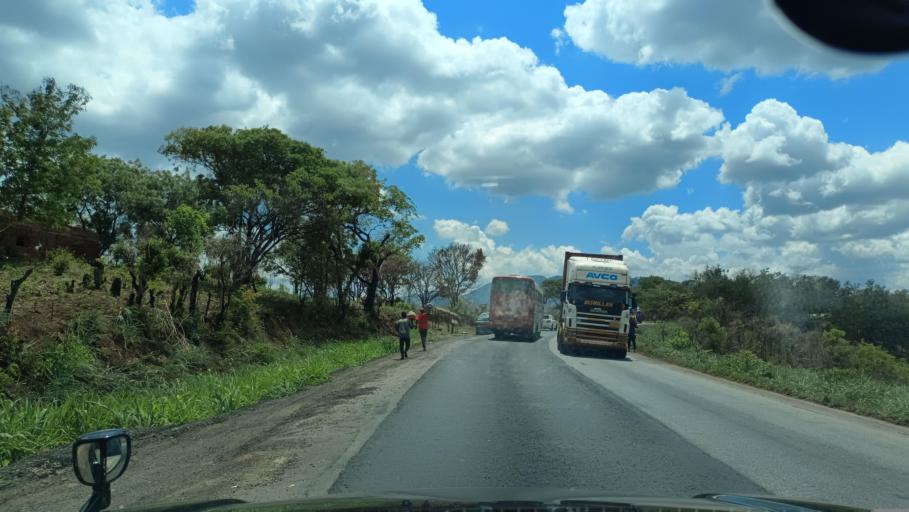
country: TZ
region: Morogoro
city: Mikumi
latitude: -7.4580
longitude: 36.9201
